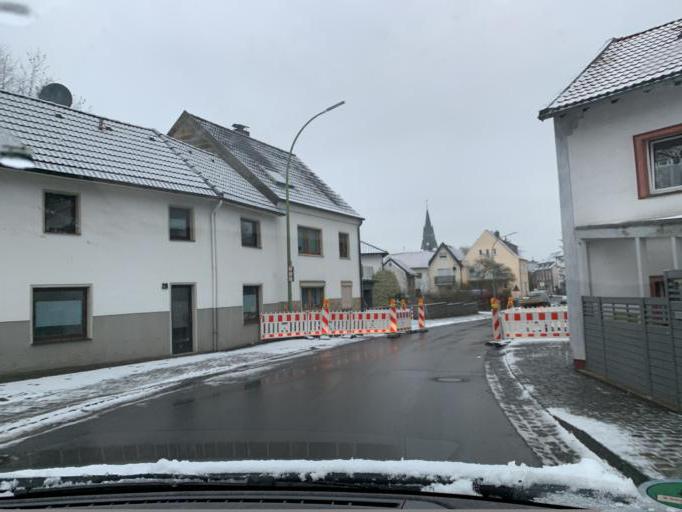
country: DE
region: North Rhine-Westphalia
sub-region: Regierungsbezirk Koln
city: Langerwehe
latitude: 50.7682
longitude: 6.3260
